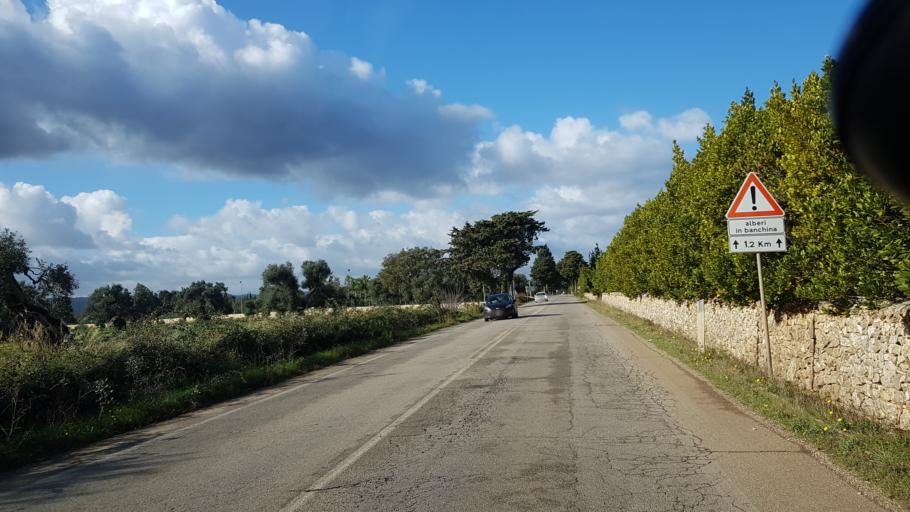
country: IT
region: Apulia
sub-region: Provincia di Brindisi
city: Pezze di Greco
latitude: 40.7999
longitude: 17.4415
